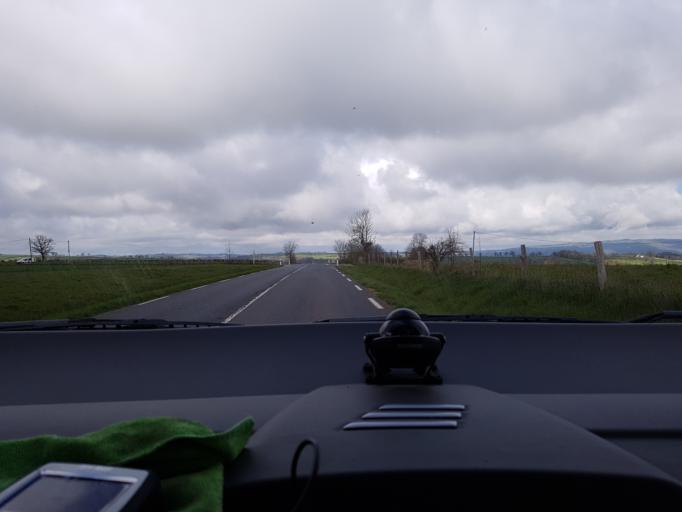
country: FR
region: Midi-Pyrenees
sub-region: Departement de l'Aveyron
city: Druelle
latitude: 44.3701
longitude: 2.4724
